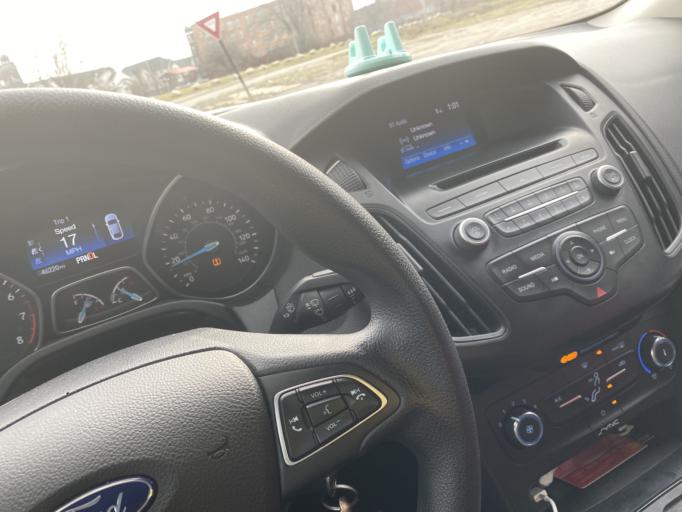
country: US
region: Michigan
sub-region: Wayne County
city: Highland Park
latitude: 42.3658
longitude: -83.1221
